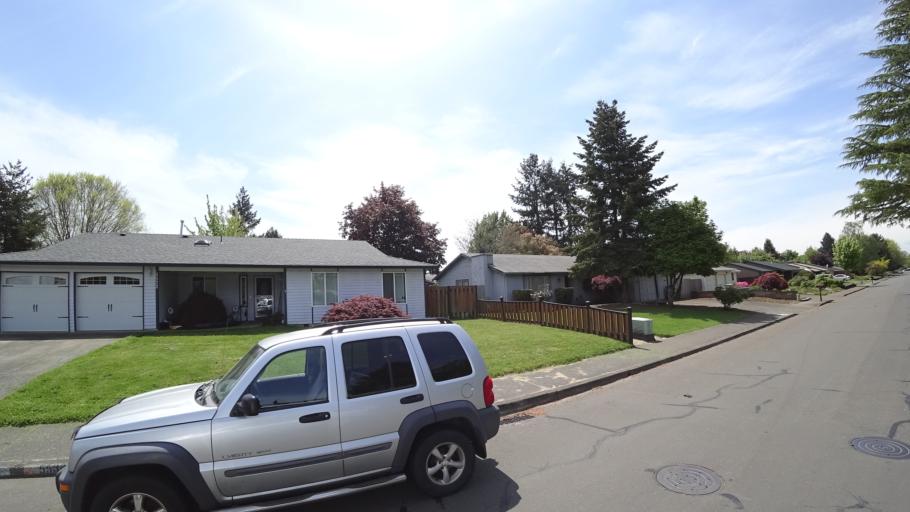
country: US
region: Oregon
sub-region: Washington County
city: Aloha
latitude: 45.5028
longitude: -122.9257
